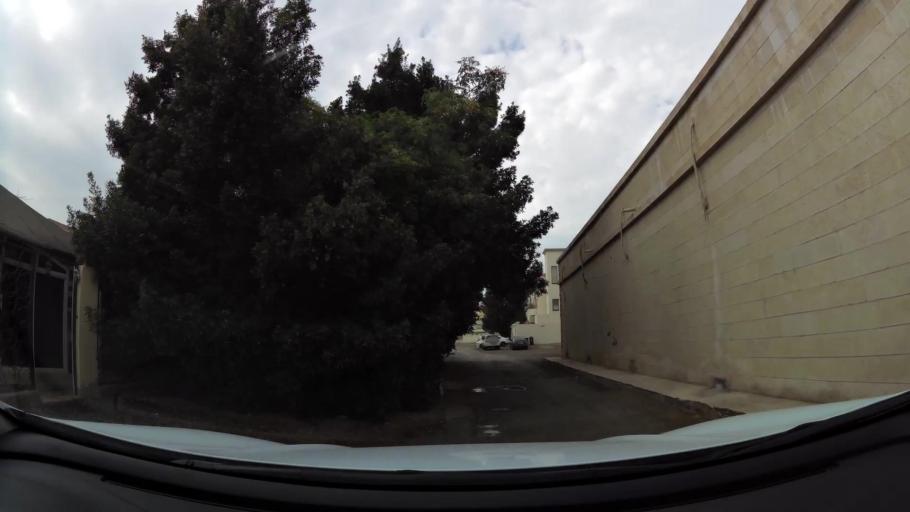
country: AE
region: Abu Dhabi
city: Abu Dhabi
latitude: 24.4287
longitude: 54.4033
